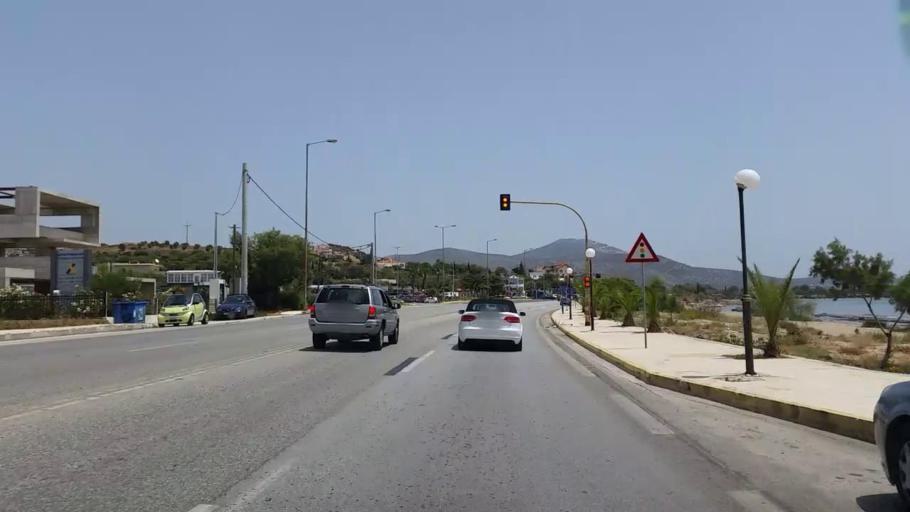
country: GR
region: Attica
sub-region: Nomarchia Anatolikis Attikis
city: Agios Dimitrios Kropias
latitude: 37.7886
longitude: 23.8839
